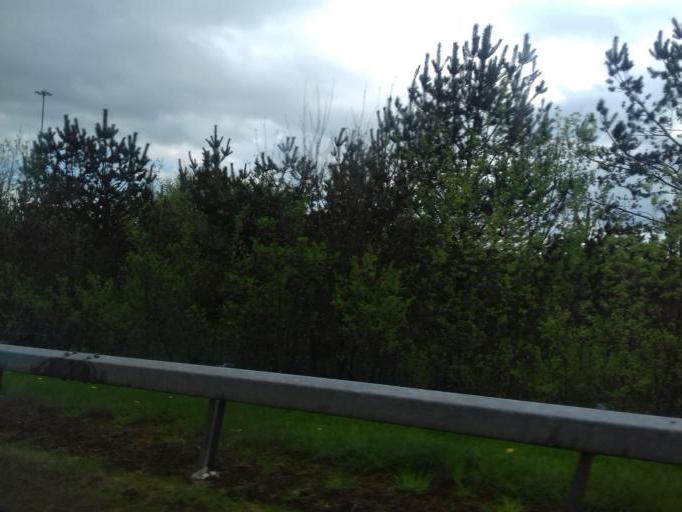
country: IE
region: Leinster
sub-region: Kildare
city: Kildare
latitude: 53.1523
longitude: -6.9177
